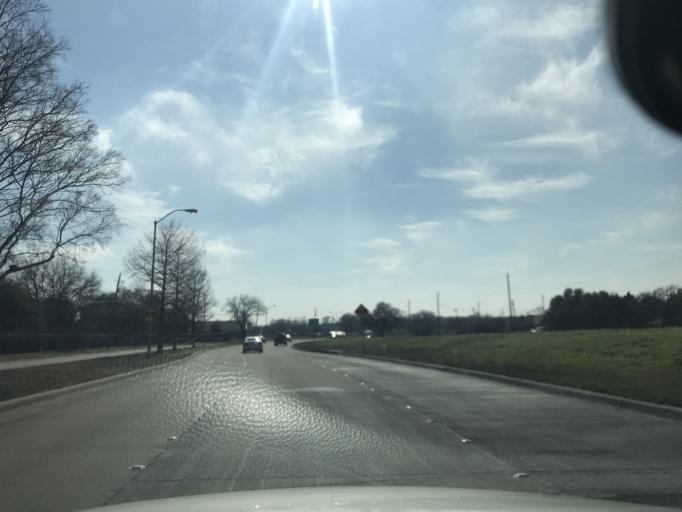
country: US
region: Texas
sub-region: Collin County
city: Parker
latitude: 33.0461
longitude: -96.6595
